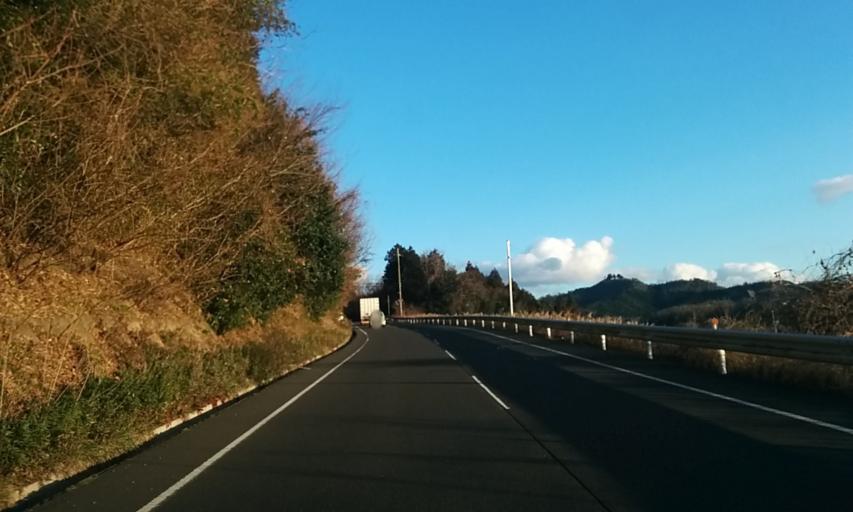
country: JP
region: Kyoto
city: Ayabe
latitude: 35.3092
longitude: 135.2666
